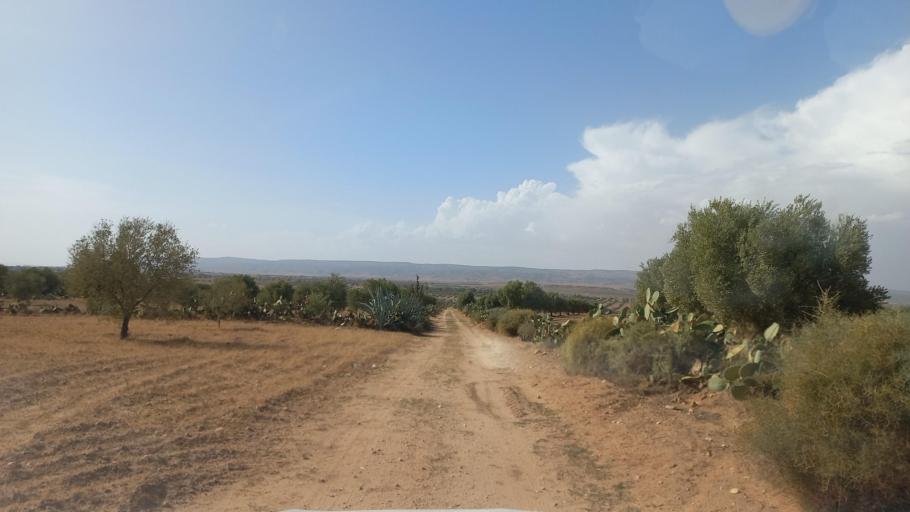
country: TN
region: Al Qasrayn
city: Kasserine
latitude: 35.2115
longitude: 8.9536
